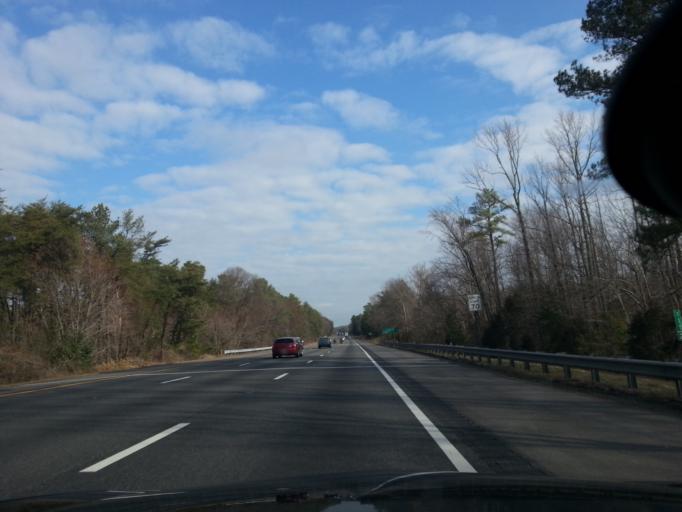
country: US
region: Virginia
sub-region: Caroline County
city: Bowling Green
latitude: 38.0277
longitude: -77.4989
